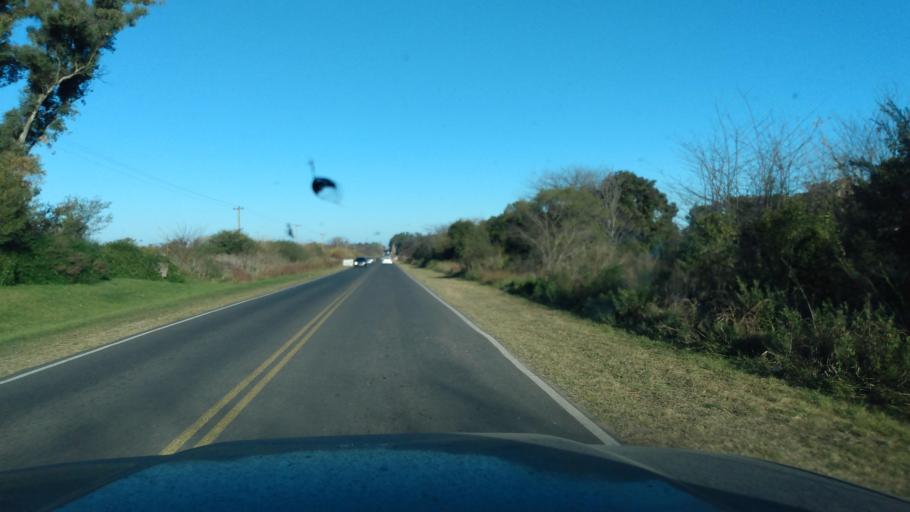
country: AR
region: Buenos Aires
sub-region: Partido de Lujan
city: Lujan
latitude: -34.5203
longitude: -59.1759
